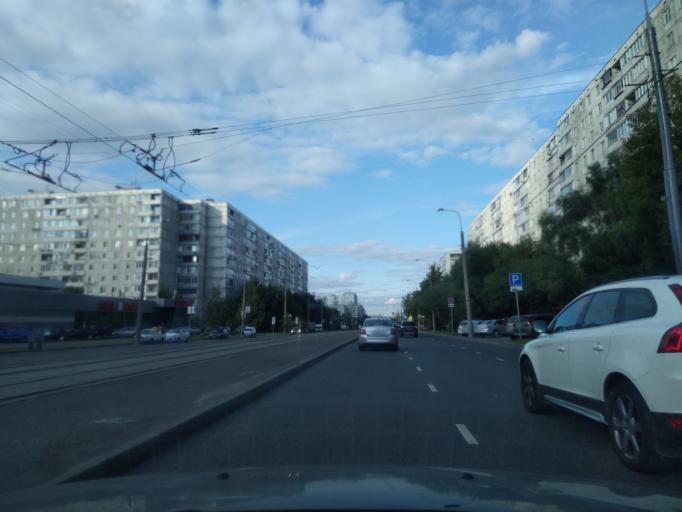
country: RU
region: Moscow
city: Strogino
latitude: 55.8082
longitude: 37.3960
